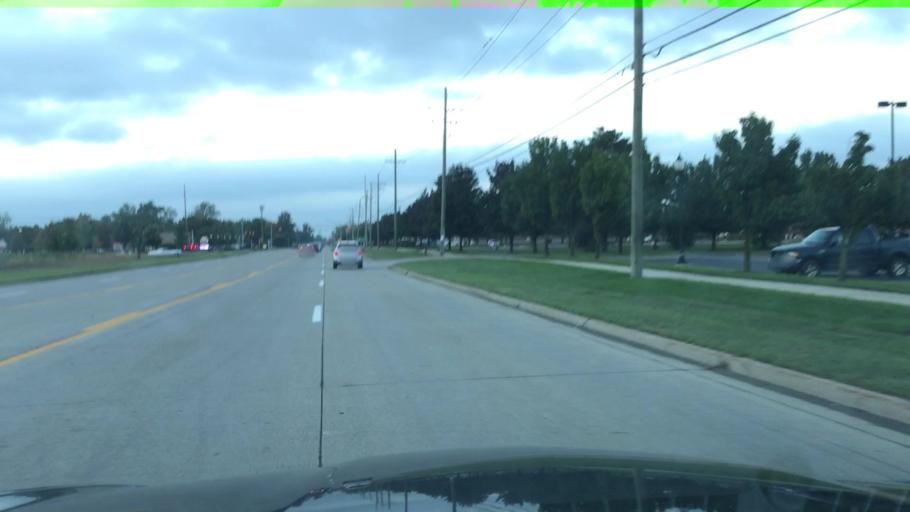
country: US
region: Michigan
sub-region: Macomb County
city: Shelby
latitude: 42.6674
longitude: -82.9944
